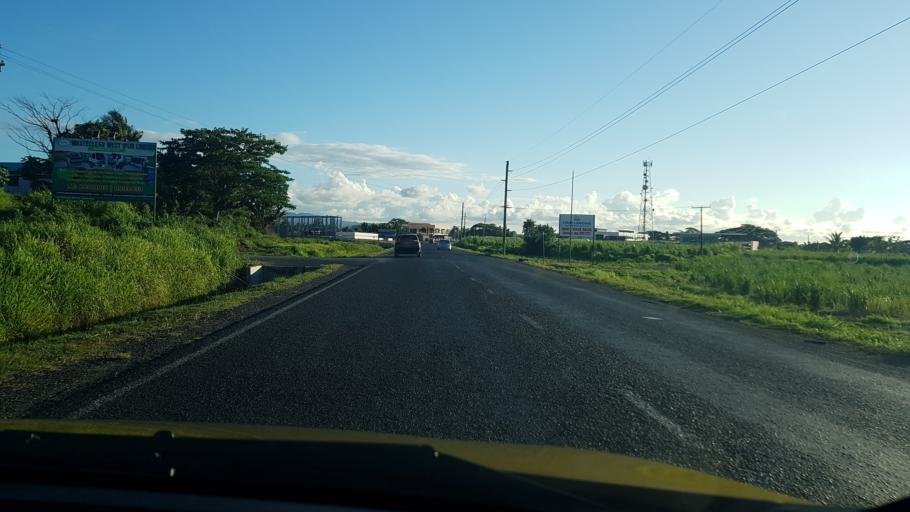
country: FJ
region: Western
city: Nadi
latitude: -17.7765
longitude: 177.4550
